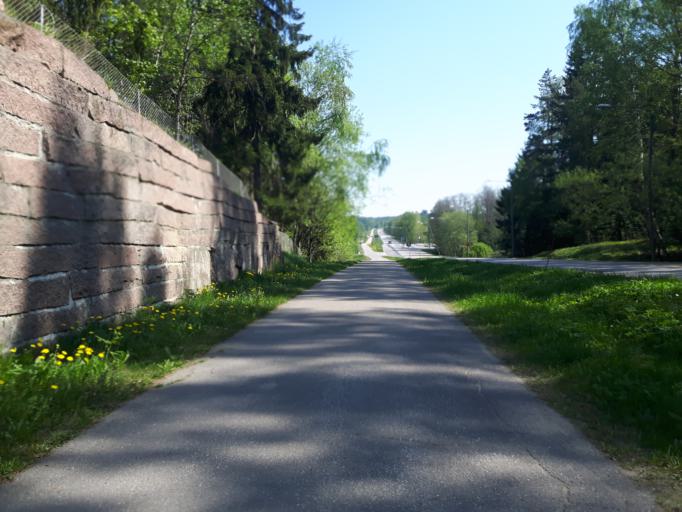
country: FI
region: Uusimaa
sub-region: Helsinki
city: Sibbo
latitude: 60.2541
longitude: 25.1880
